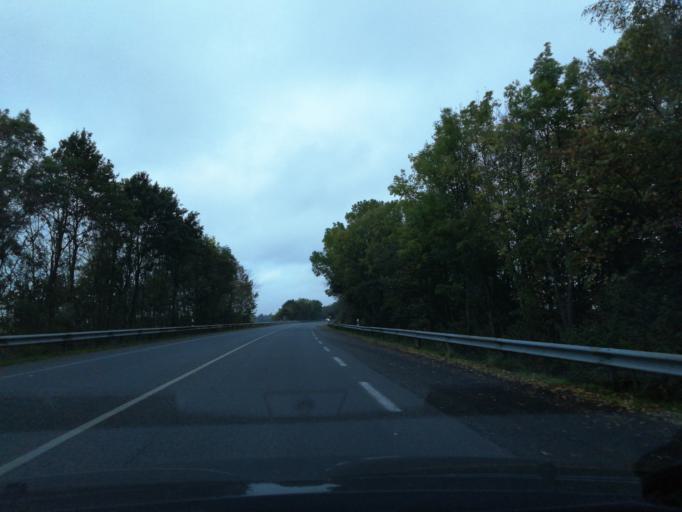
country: DE
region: Lower Saxony
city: Fedderwarden
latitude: 53.5490
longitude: 8.0474
